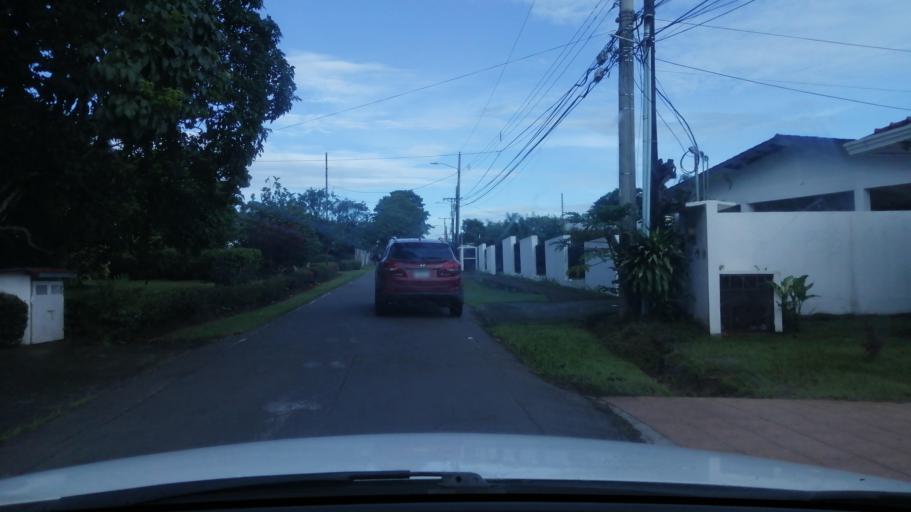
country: PA
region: Chiriqui
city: Mata del Nance
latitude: 8.4530
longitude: -82.4179
